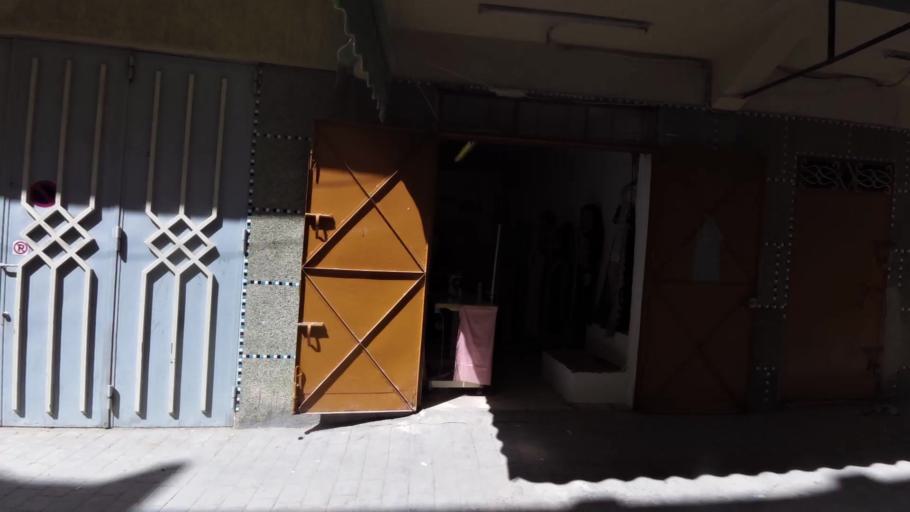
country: MA
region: Tanger-Tetouan
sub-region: Tanger-Assilah
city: Tangier
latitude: 35.7516
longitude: -5.8185
